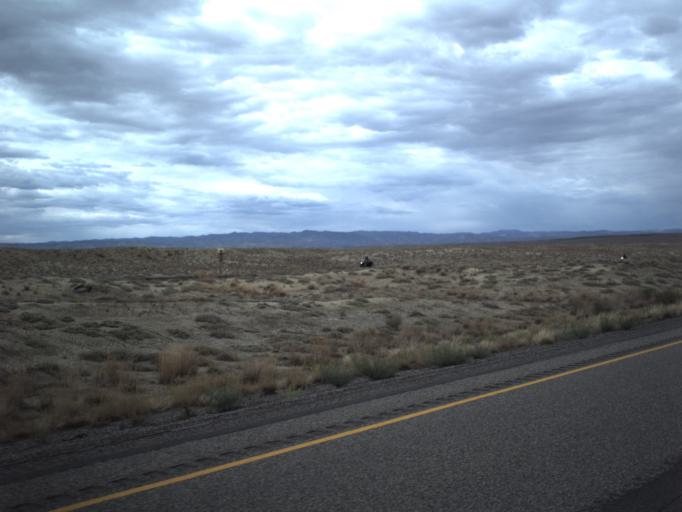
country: US
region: Colorado
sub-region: Mesa County
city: Loma
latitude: 39.1070
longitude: -109.1924
